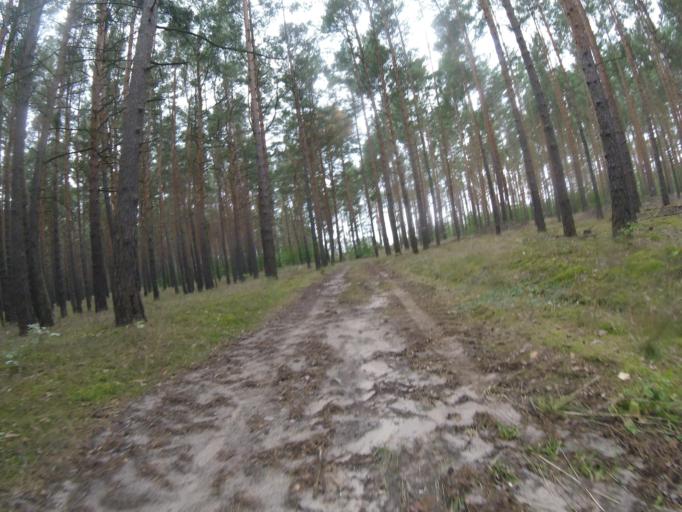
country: DE
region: Brandenburg
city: Bestensee
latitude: 52.2214
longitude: 13.6782
